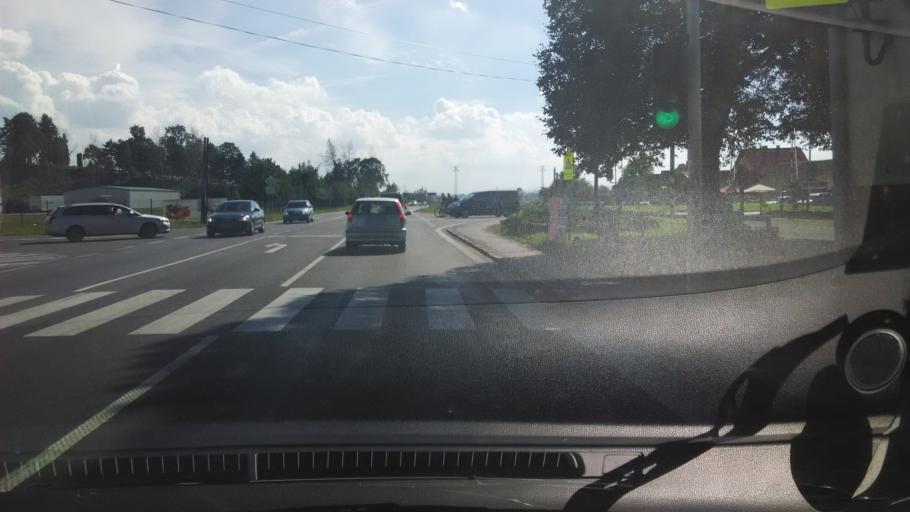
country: SK
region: Zilinsky
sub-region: Okres Martin
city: Martin
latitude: 49.0289
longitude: 18.9061
